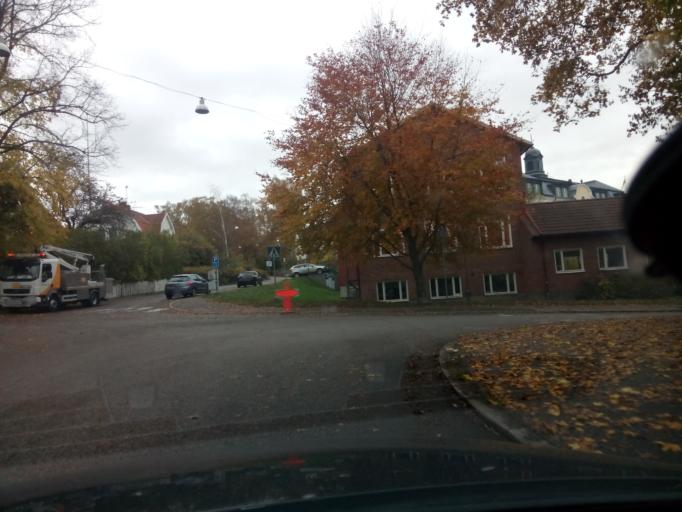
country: SE
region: Soedermanland
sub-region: Nykopings Kommun
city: Nykoping
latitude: 58.7566
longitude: 17.0193
